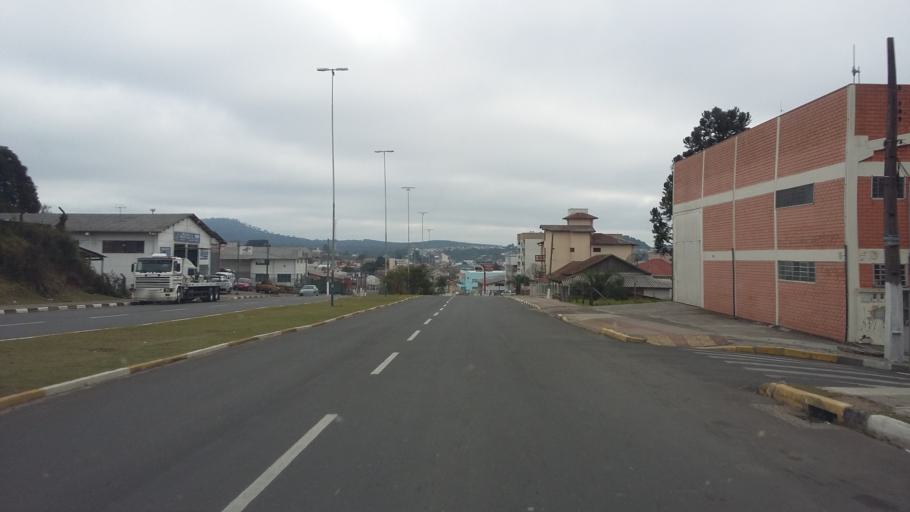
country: BR
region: Santa Catarina
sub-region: Lages
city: Lages
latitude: -27.8278
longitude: -50.3381
